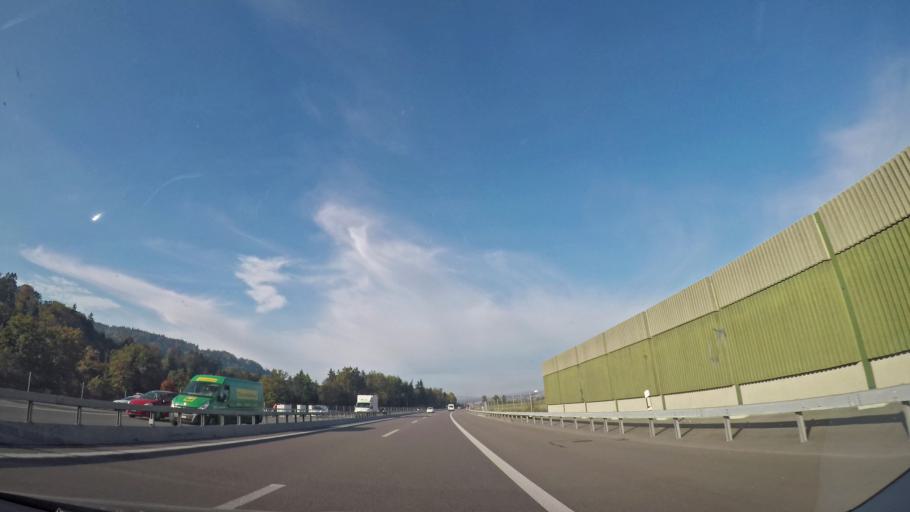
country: CH
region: Bern
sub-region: Bern-Mittelland District
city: Niederwichtrach
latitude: 46.8405
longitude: 7.5602
